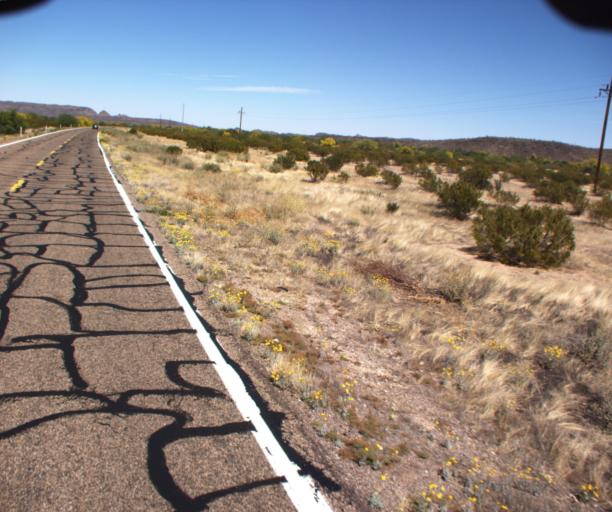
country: US
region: Arizona
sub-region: Pima County
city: Ajo
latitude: 32.4886
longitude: -112.8811
